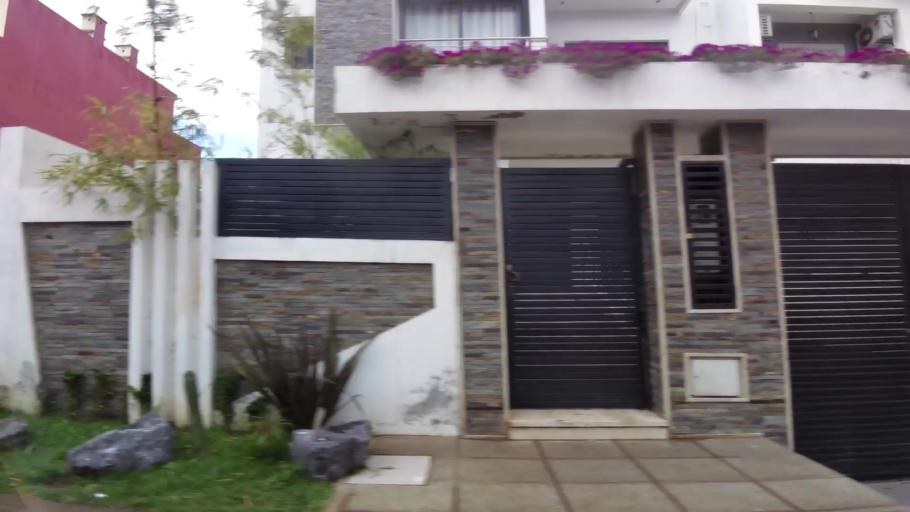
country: MA
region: Grand Casablanca
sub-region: Nouaceur
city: Bouskoura
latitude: 33.5167
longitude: -7.6392
